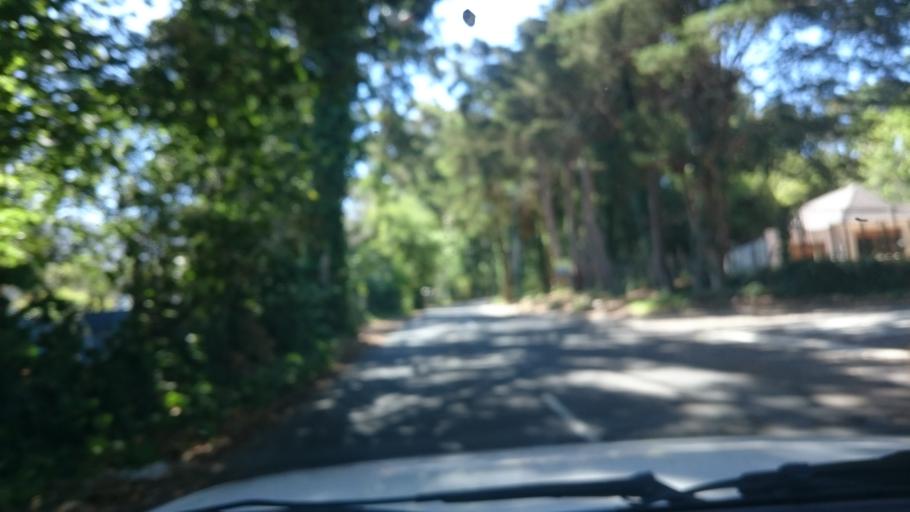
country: ZA
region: Western Cape
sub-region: City of Cape Town
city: Newlands
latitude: -33.9997
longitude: 18.4483
